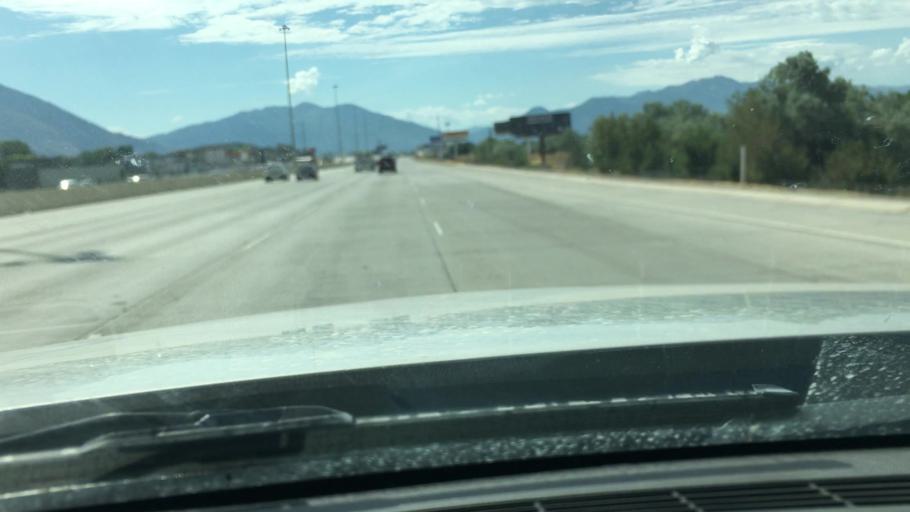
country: US
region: Utah
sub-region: Utah County
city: Orem
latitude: 40.2702
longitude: -111.7150
